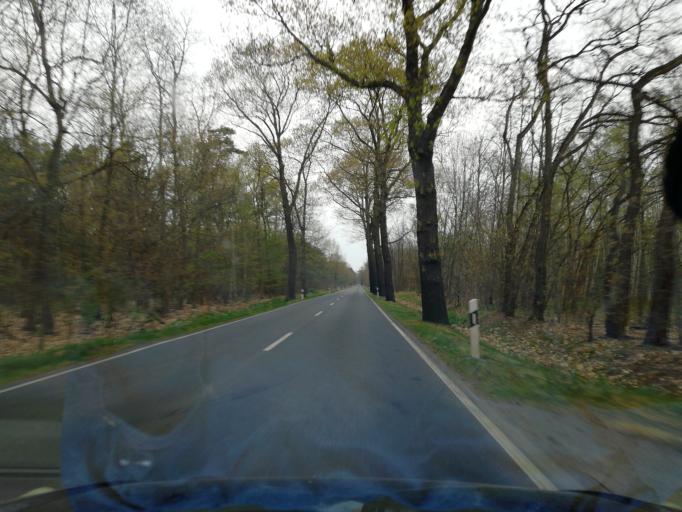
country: DE
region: Brandenburg
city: Calau
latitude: 51.7761
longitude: 13.8922
